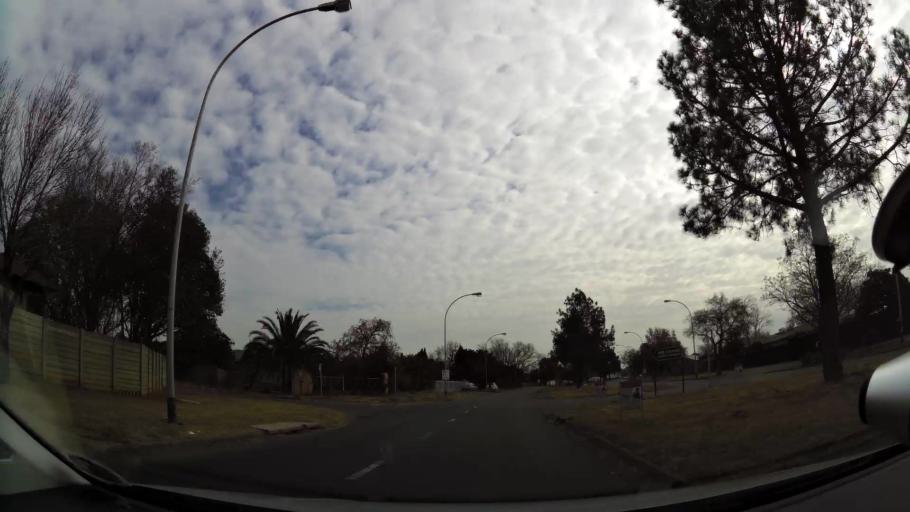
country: ZA
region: Orange Free State
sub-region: Mangaung Metropolitan Municipality
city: Bloemfontein
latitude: -29.1286
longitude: 26.1779
